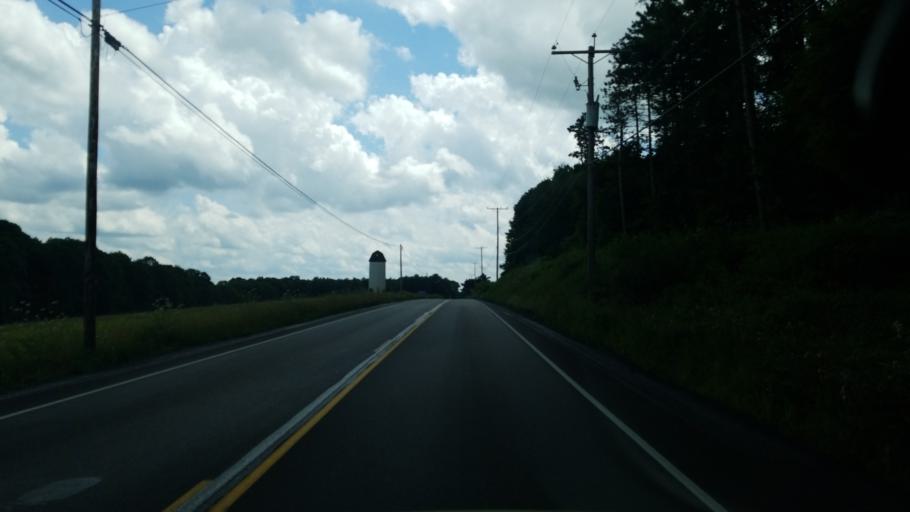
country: US
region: Pennsylvania
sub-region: Jefferson County
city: Brookville
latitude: 41.2299
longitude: -79.1118
